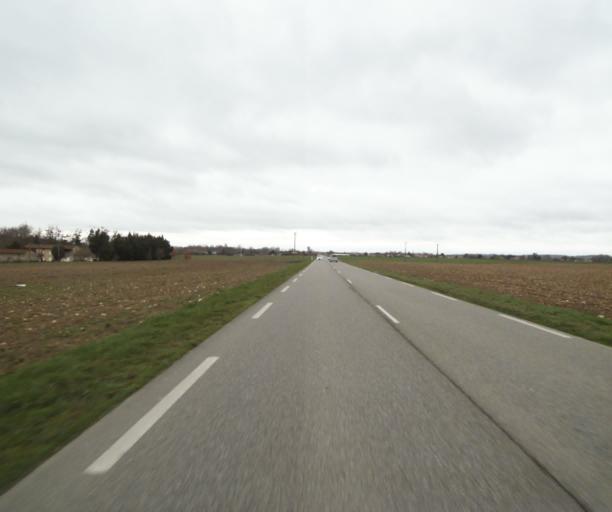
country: FR
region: Midi-Pyrenees
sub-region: Departement de l'Ariege
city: Pamiers
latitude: 43.1772
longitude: 1.6065
